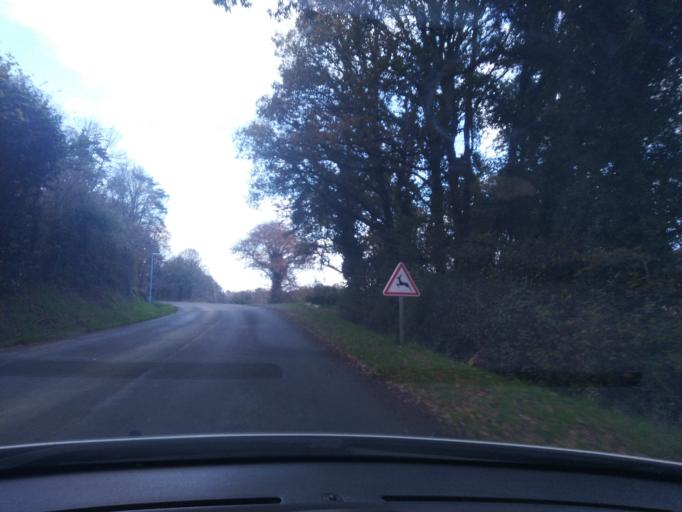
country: FR
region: Brittany
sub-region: Departement du Finistere
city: Plouigneau
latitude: 48.5678
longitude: -3.6394
